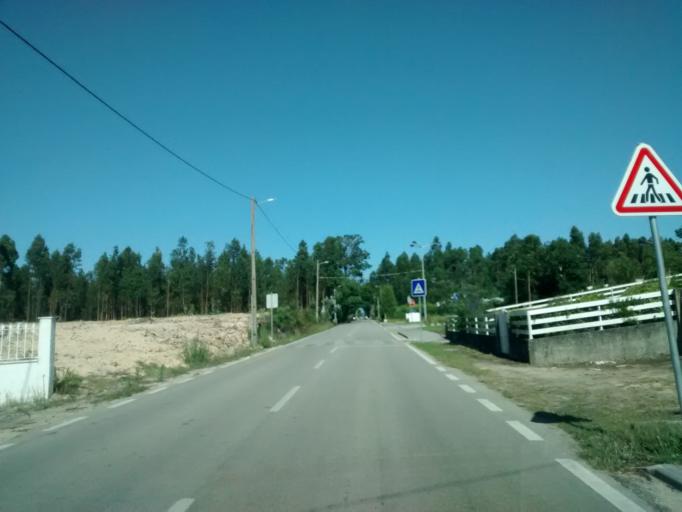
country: PT
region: Coimbra
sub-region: Cantanhede
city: Cantanhede
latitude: 40.4191
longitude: -8.5553
